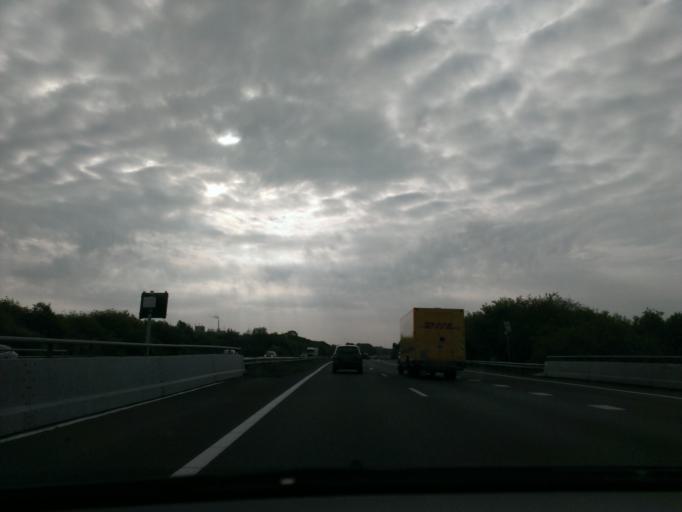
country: NL
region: Overijssel
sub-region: Gemeente Staphorst
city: Staphorst
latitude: 52.6846
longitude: 6.2686
